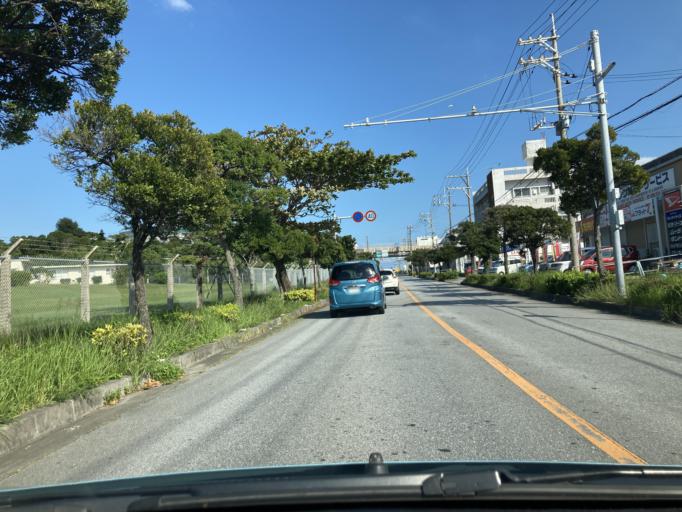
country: JP
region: Okinawa
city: Chatan
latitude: 26.3007
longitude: 127.7908
